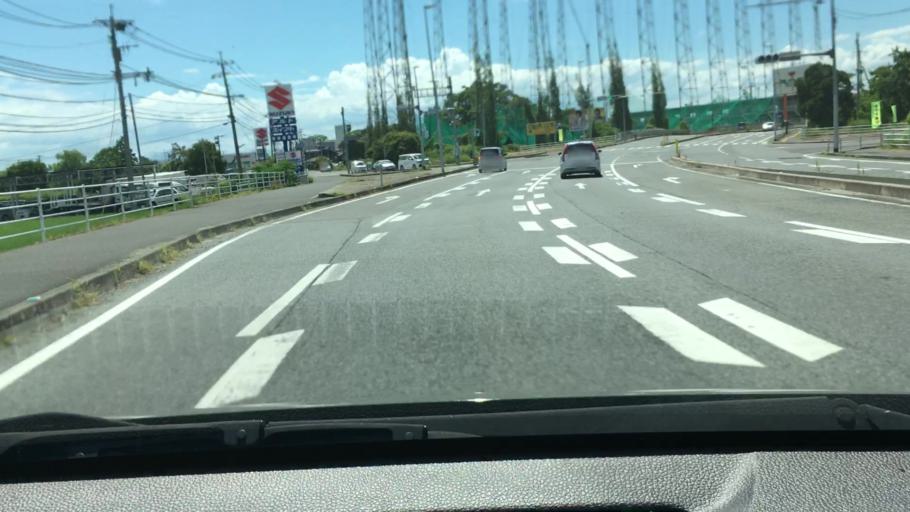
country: JP
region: Saga Prefecture
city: Saga-shi
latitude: 33.2742
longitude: 130.3362
